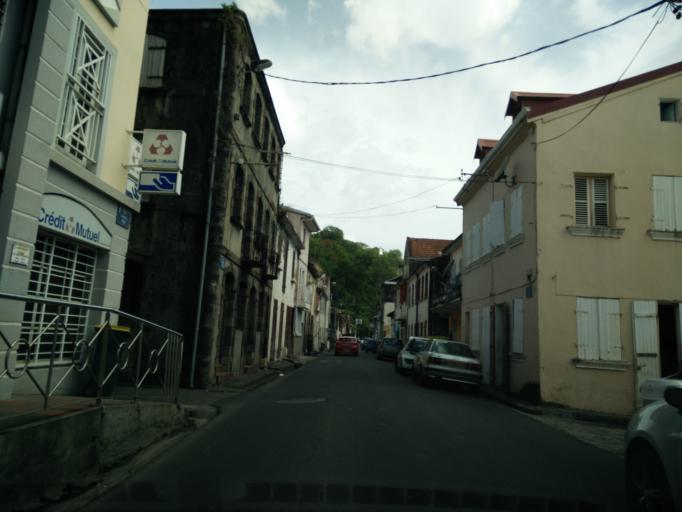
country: MQ
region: Martinique
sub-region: Martinique
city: Saint-Pierre
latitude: 14.7391
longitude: -61.1764
